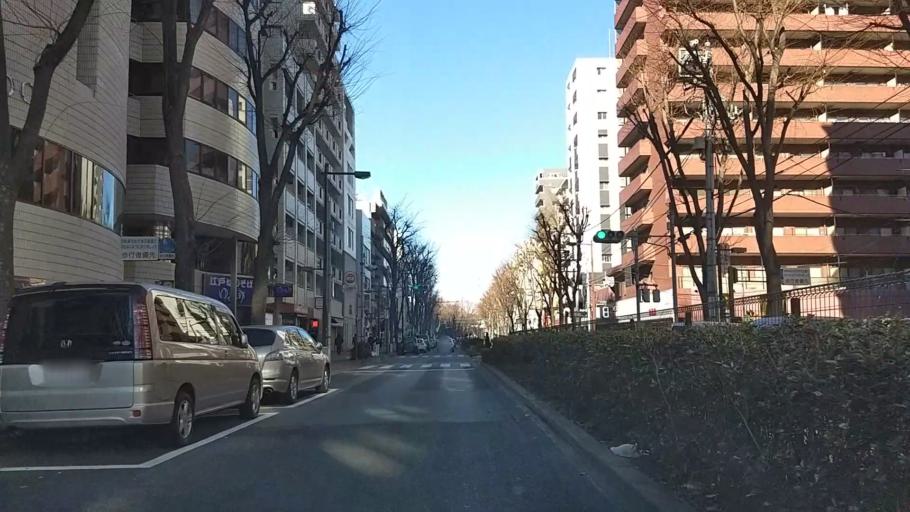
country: JP
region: Tokyo
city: Tokyo
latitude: 35.7347
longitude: 139.7095
